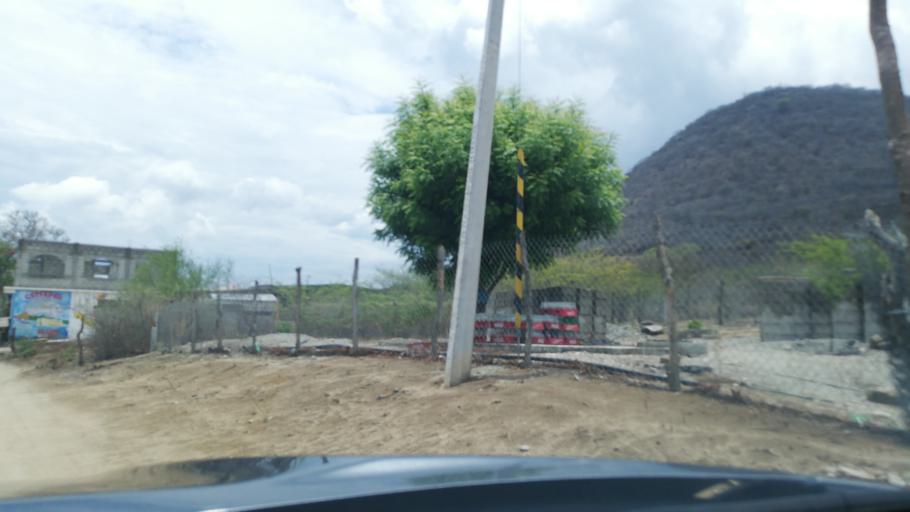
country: MX
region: Oaxaca
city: Santa Maria Jalapa del Marques
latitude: 16.4527
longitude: -95.4421
